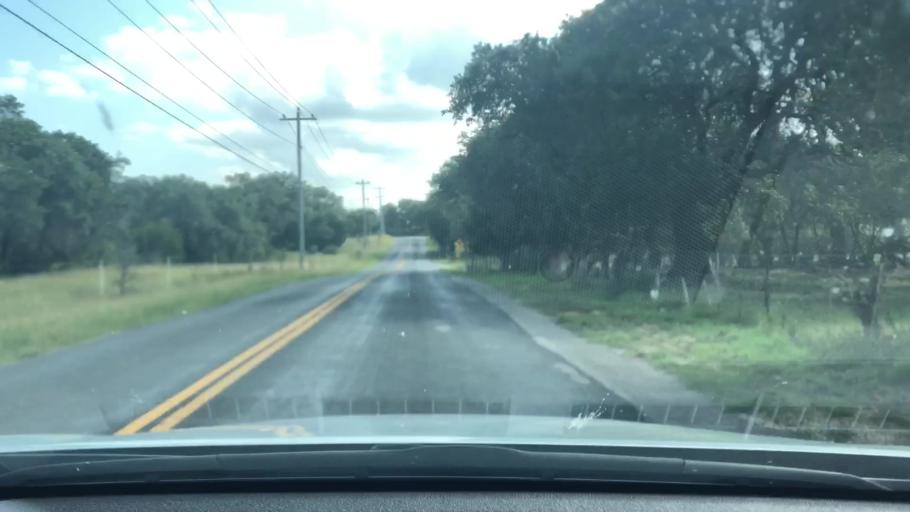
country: US
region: Texas
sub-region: Bexar County
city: Fair Oaks Ranch
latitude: 29.7727
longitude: -98.6263
